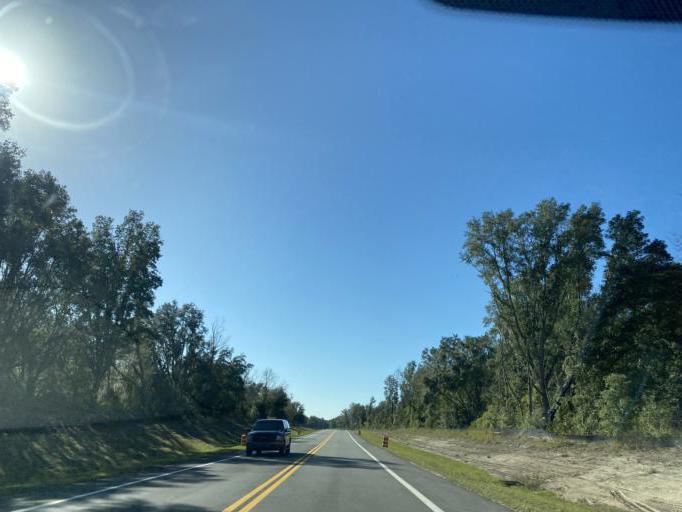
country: US
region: Florida
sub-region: Lake County
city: Mount Plymouth
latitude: 28.8220
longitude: -81.5220
